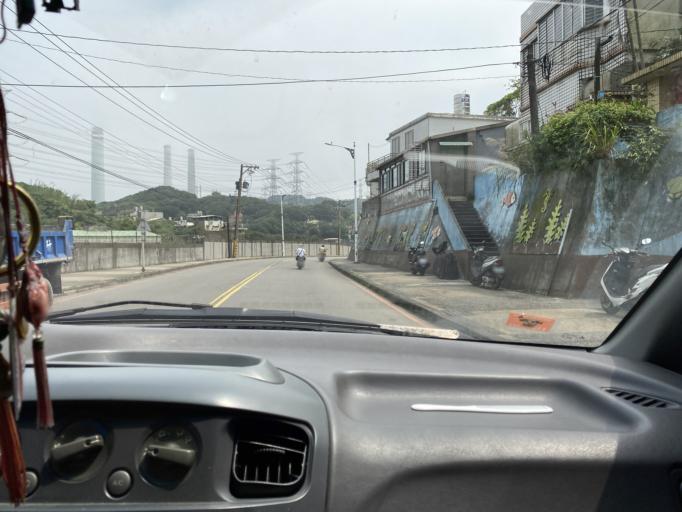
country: TW
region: Taiwan
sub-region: Keelung
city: Keelung
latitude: 25.1558
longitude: 121.7305
